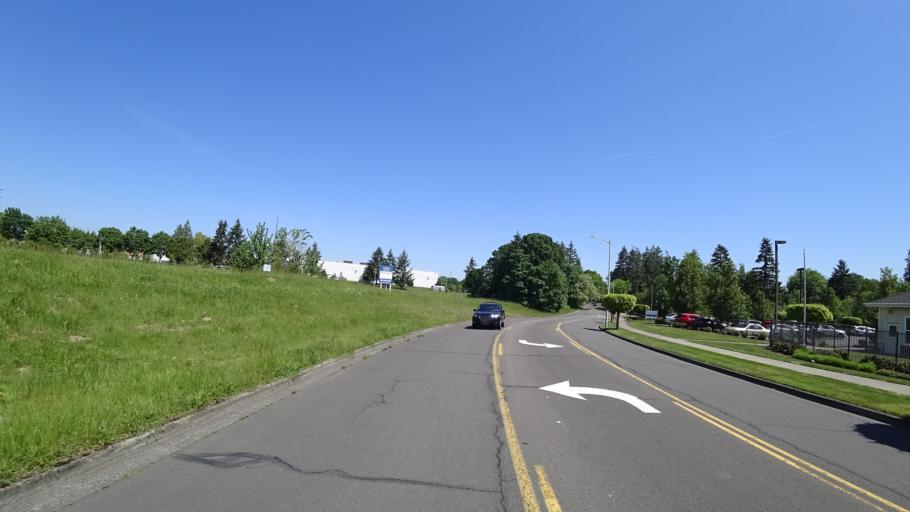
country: US
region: Oregon
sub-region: Washington County
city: Rockcreek
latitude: 45.5290
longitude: -122.9268
